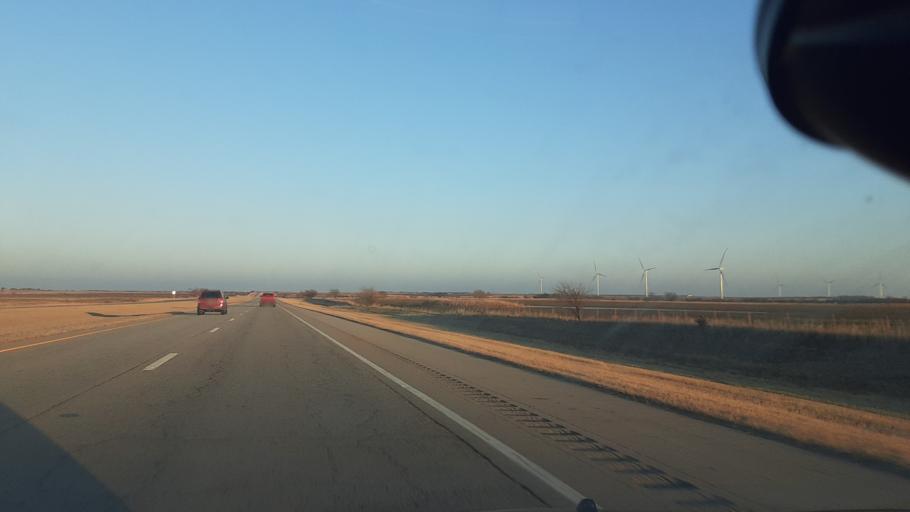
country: US
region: Oklahoma
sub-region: Noble County
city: Perry
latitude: 36.3979
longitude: -97.4049
